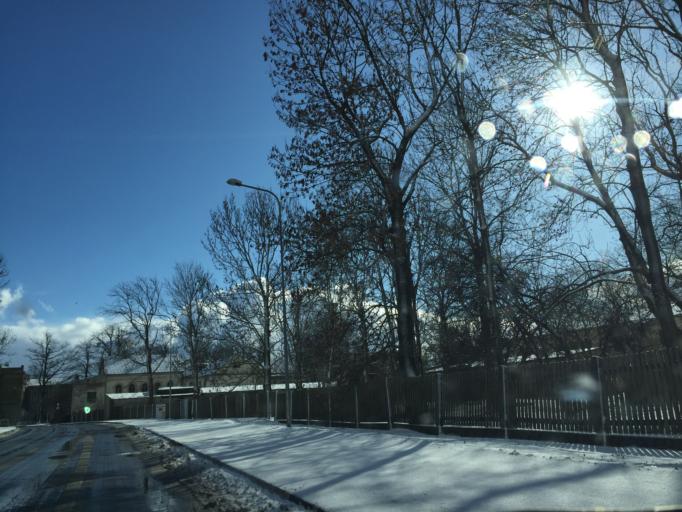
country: LV
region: Ventspils
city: Ventspils
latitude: 57.3967
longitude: 21.5709
